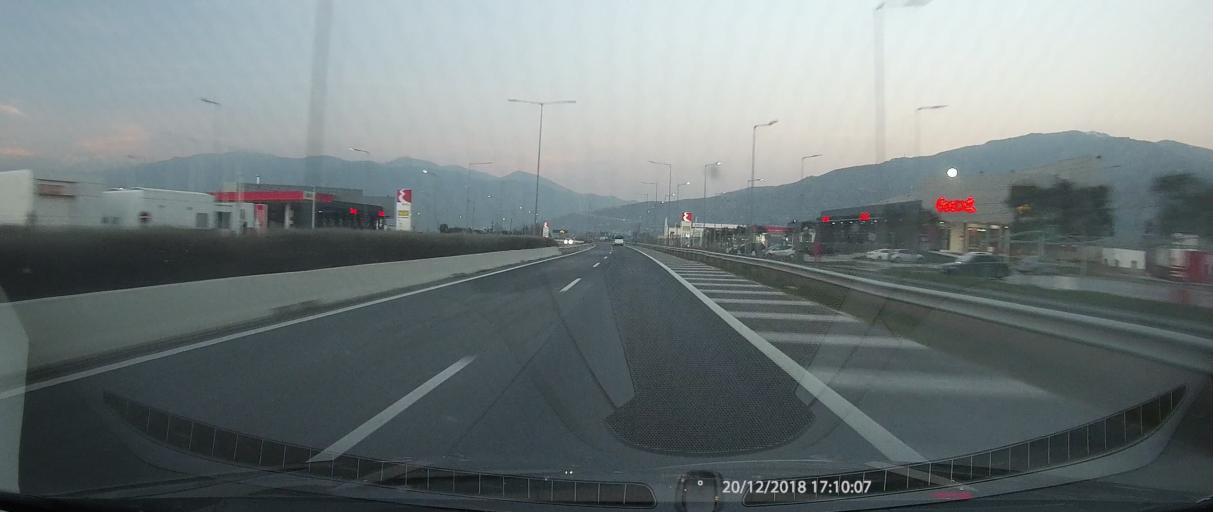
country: GR
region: Thessaly
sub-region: Nomos Larisis
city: Makrychori
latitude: 39.8135
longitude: 22.5073
